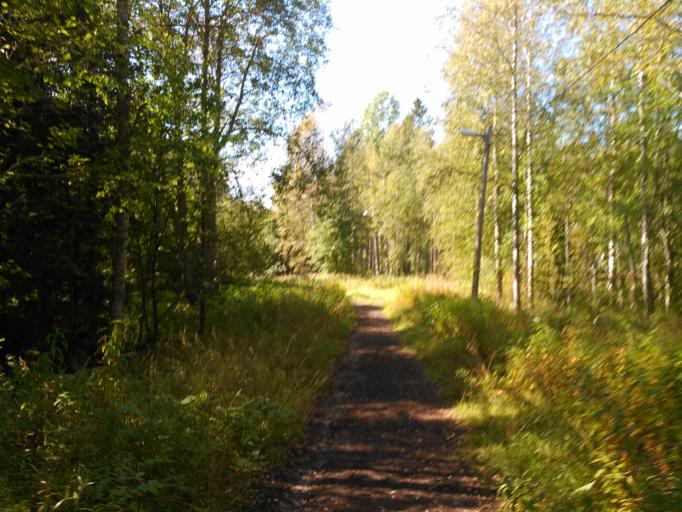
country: SE
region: Vaesterbotten
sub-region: Umea Kommun
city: Umea
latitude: 63.7947
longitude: 20.3178
